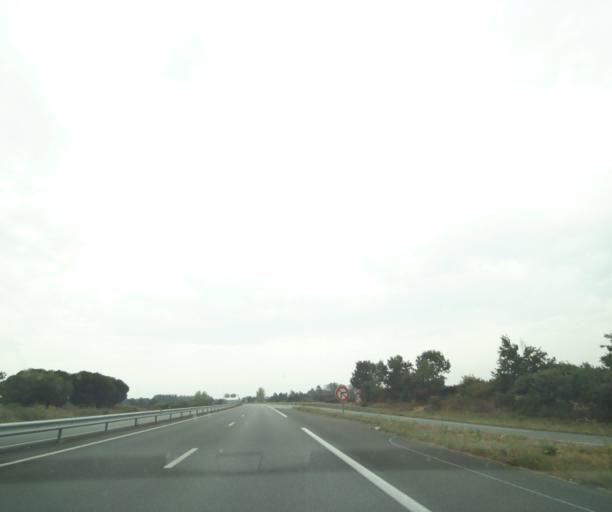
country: FR
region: Pays de la Loire
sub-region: Departement de la Vendee
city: Bournezeau
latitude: 46.6272
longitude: -1.1482
